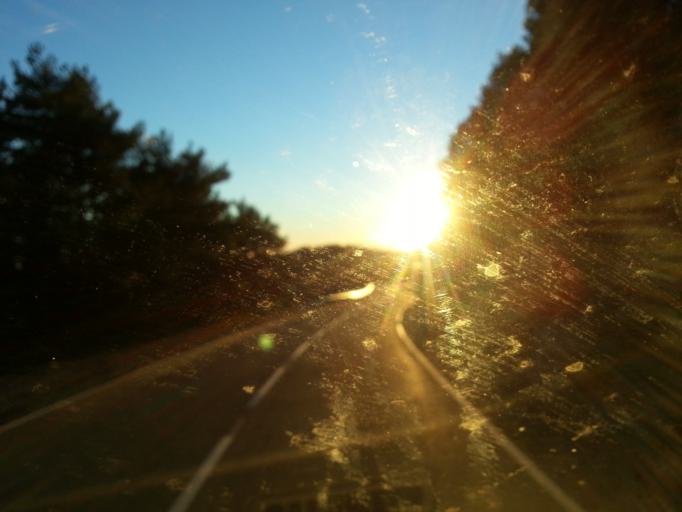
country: ES
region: Catalonia
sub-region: Provincia de Lleida
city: Olius
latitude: 42.1425
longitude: 1.5497
